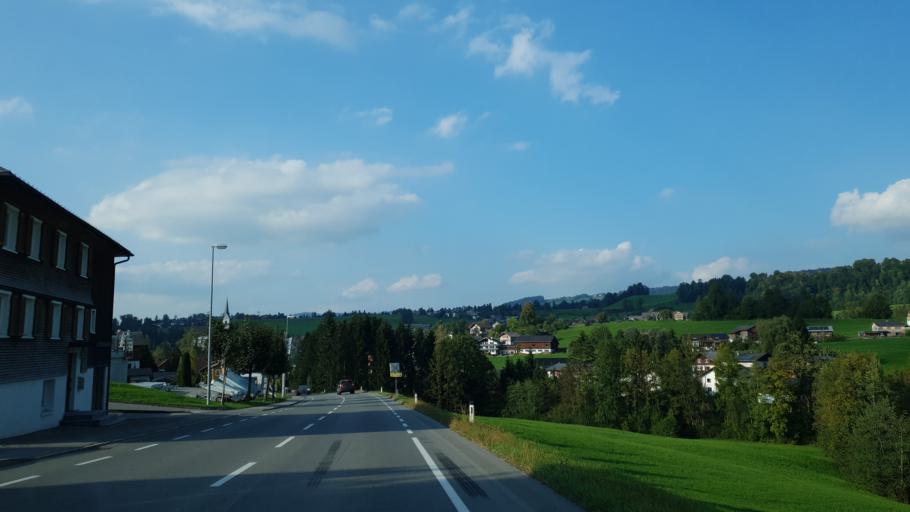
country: AT
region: Vorarlberg
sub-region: Politischer Bezirk Bregenz
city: Egg
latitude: 47.4246
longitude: 9.8979
